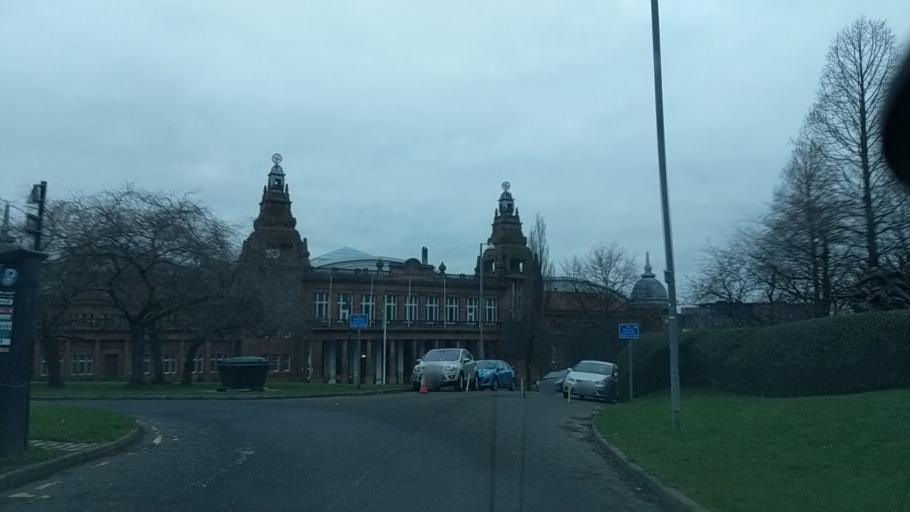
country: GB
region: Scotland
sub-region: Glasgow City
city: Glasgow
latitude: 55.8694
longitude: -4.2917
